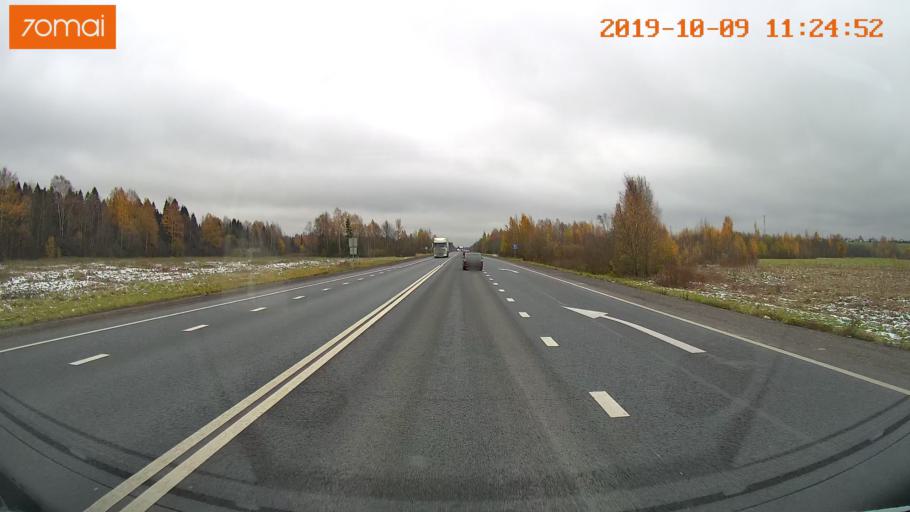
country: RU
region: Vologda
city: Vologda
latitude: 59.1072
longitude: 39.9847
